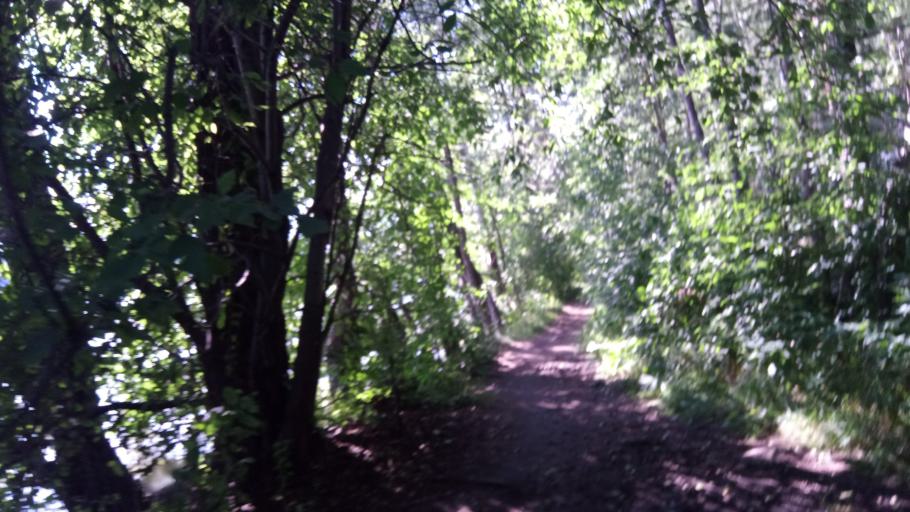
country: RU
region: Chelyabinsk
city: Chebarkul'
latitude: 55.0156
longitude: 60.3141
